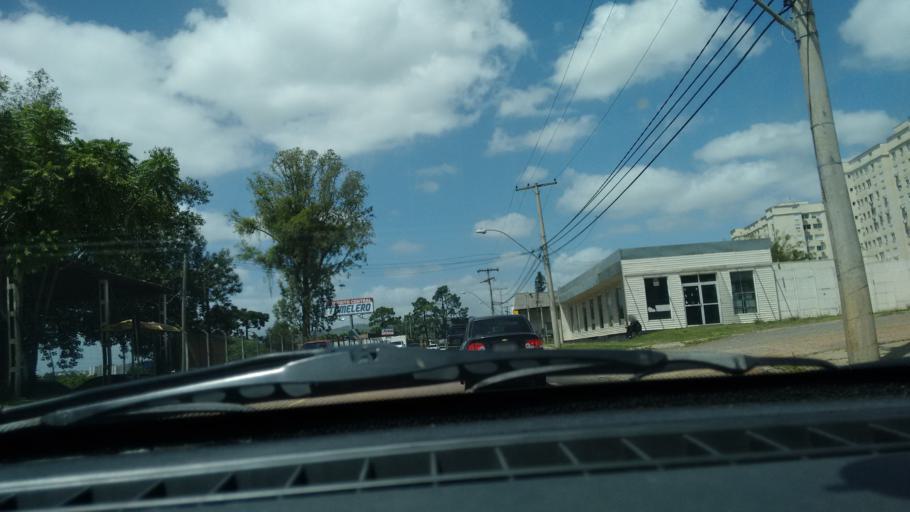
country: BR
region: Rio Grande do Sul
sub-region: Cachoeirinha
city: Cachoeirinha
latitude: -30.0051
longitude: -51.1277
